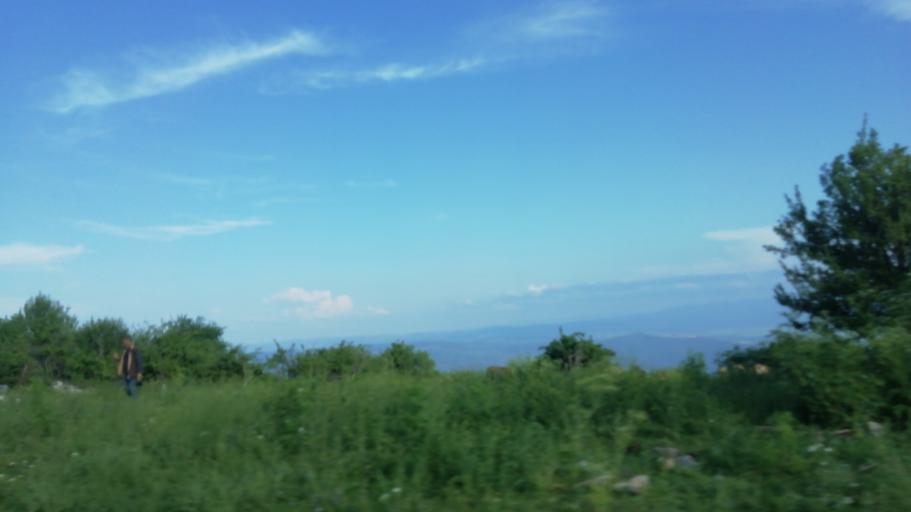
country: TR
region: Karabuk
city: Eskipazar
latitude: 41.0454
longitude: 32.5584
